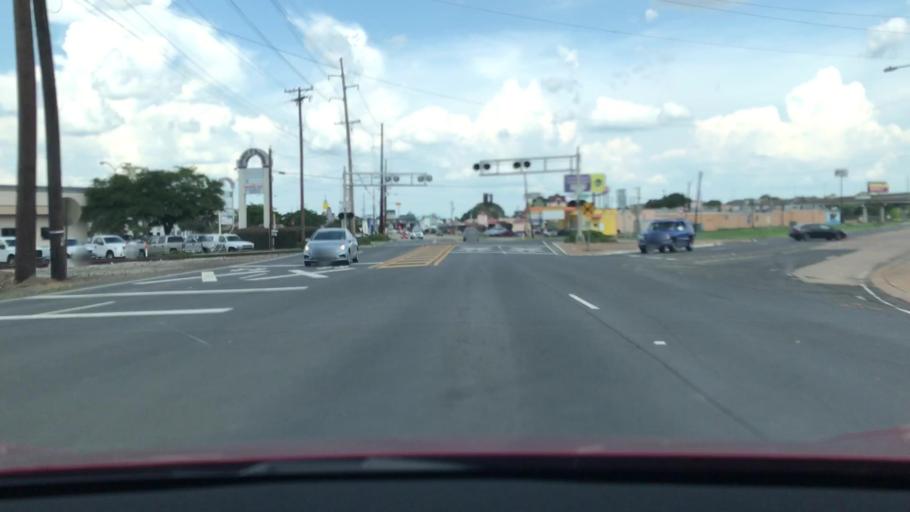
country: US
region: Louisiana
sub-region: Bossier Parish
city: Bossier City
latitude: 32.5158
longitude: -93.7202
